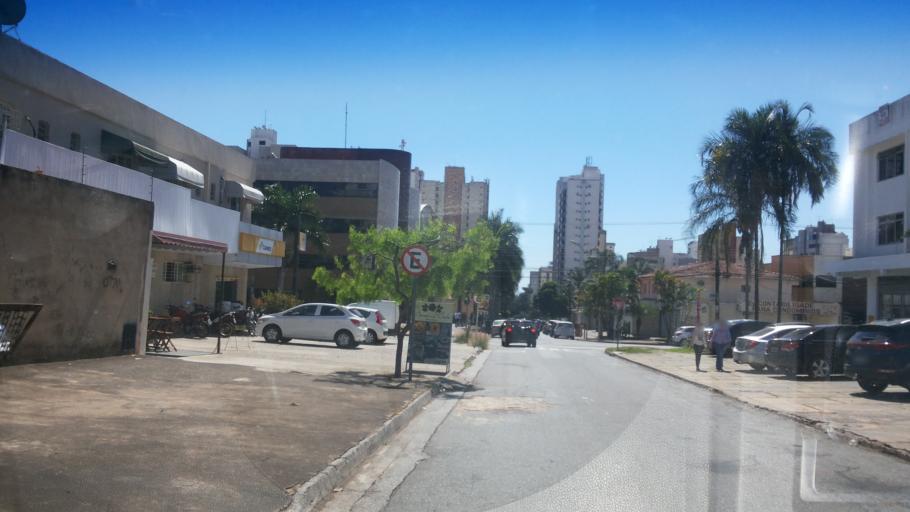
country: BR
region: Goias
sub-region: Goiania
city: Goiania
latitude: -16.7196
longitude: -49.2618
